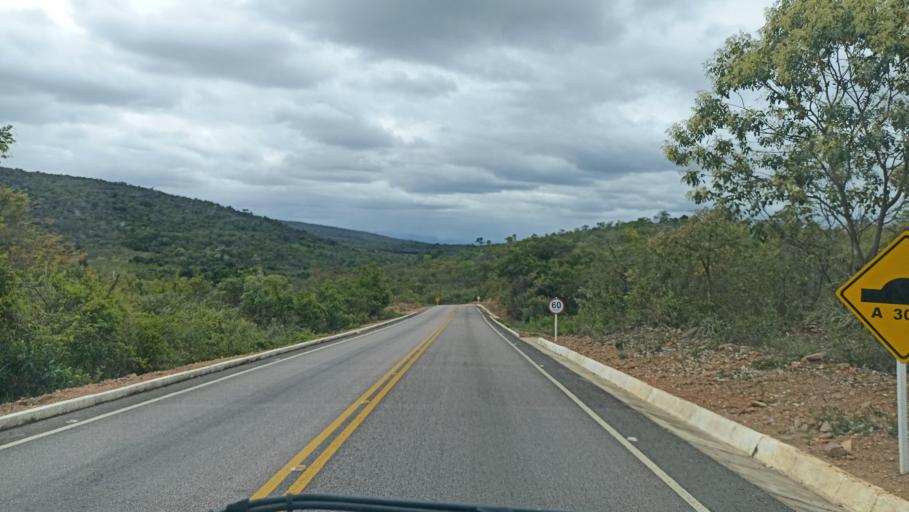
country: BR
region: Bahia
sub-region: Andarai
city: Vera Cruz
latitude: -12.9264
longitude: -41.2312
